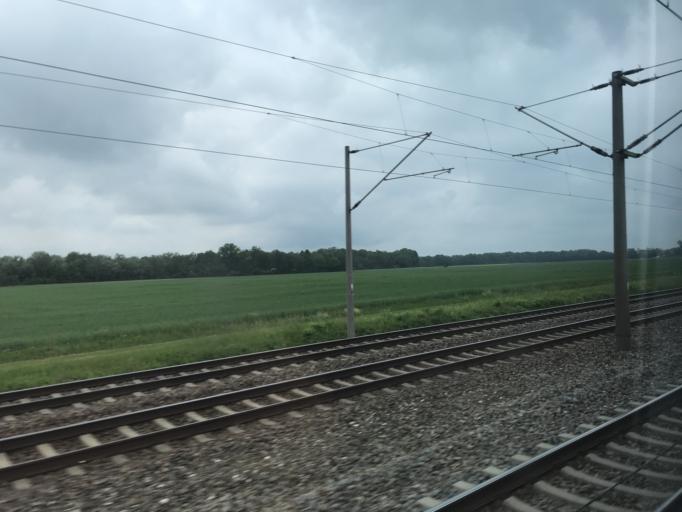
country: DE
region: Bavaria
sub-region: Swabia
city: Kissing
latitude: 48.3261
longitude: 10.9552
